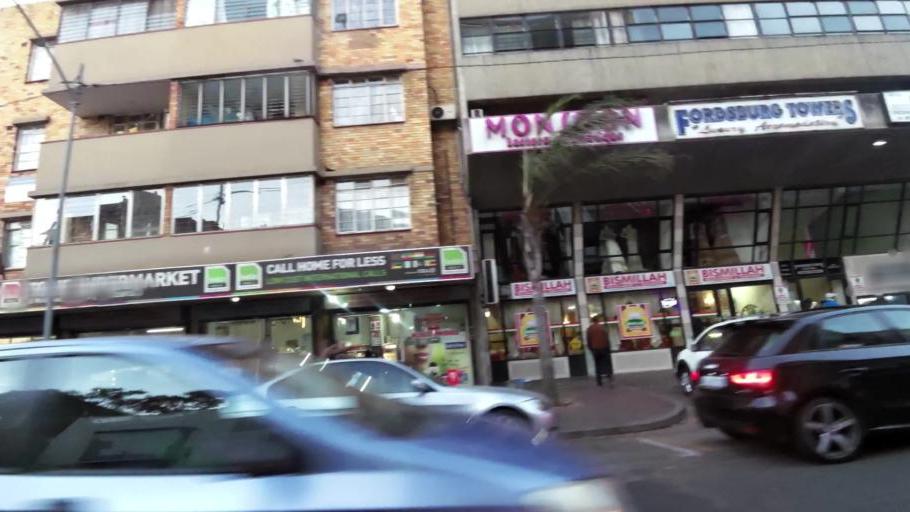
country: ZA
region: Gauteng
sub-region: City of Johannesburg Metropolitan Municipality
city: Johannesburg
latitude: -26.2017
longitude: 28.0216
